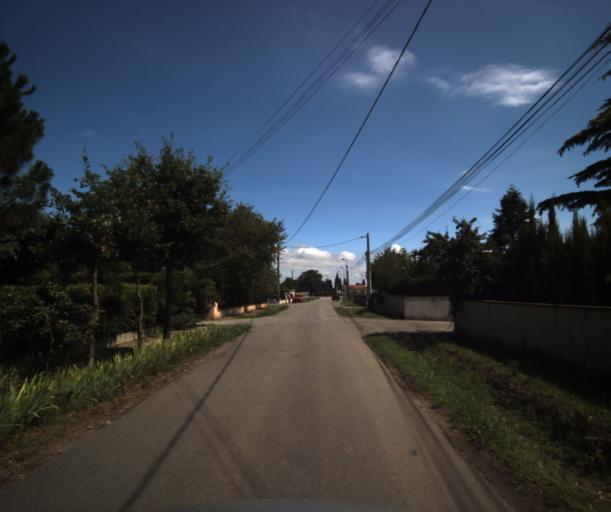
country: FR
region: Midi-Pyrenees
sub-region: Departement de la Haute-Garonne
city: Lacasse
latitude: 43.3907
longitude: 1.2597
